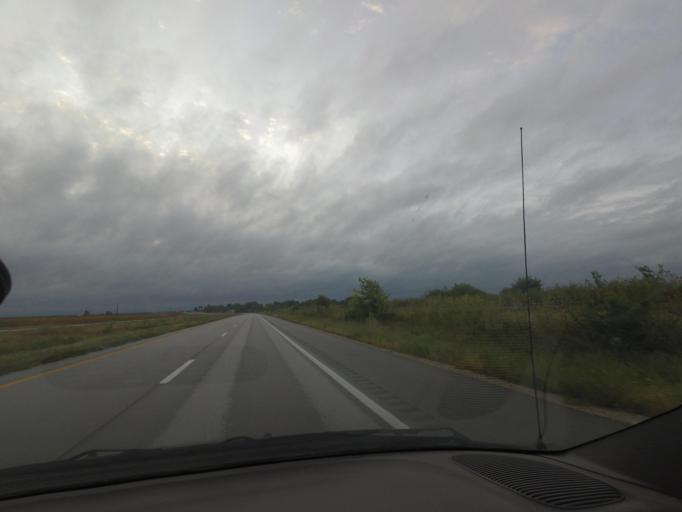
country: US
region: Missouri
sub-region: Shelby County
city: Shelbina
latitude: 39.6757
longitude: -91.9628
